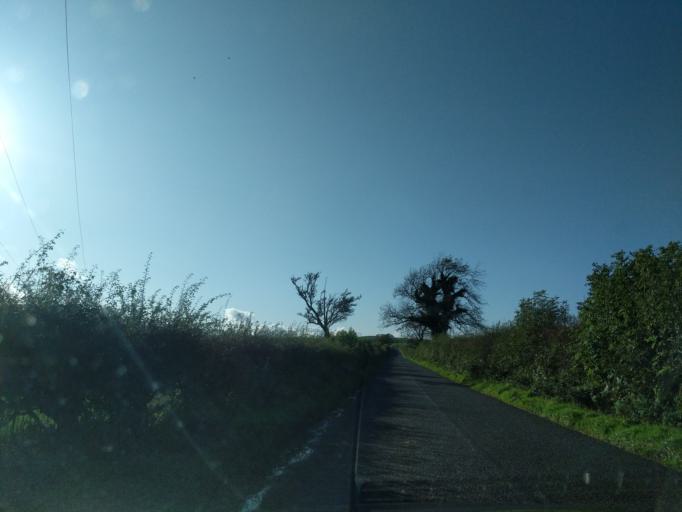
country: GB
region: Scotland
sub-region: Dumfries and Galloway
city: Dumfries
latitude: 55.0435
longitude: -3.7309
